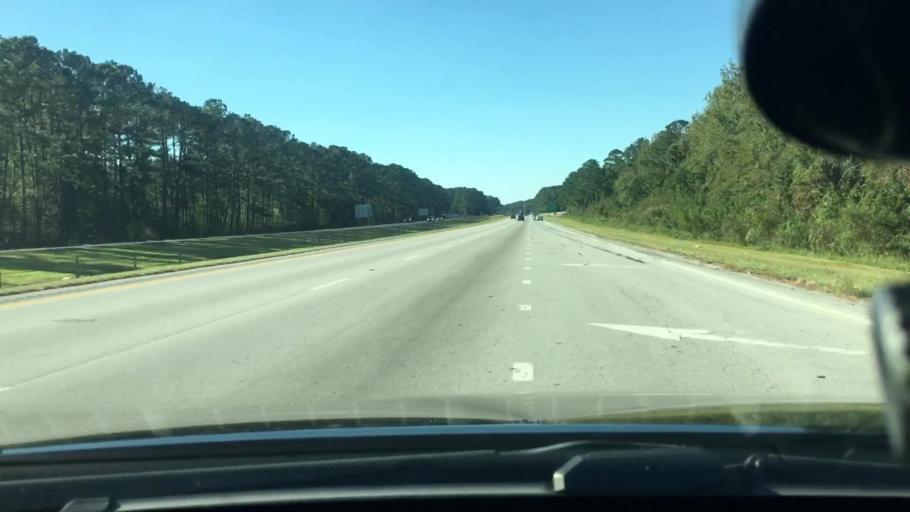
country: US
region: North Carolina
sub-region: Craven County
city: Trent Woods
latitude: 35.1071
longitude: -77.0887
